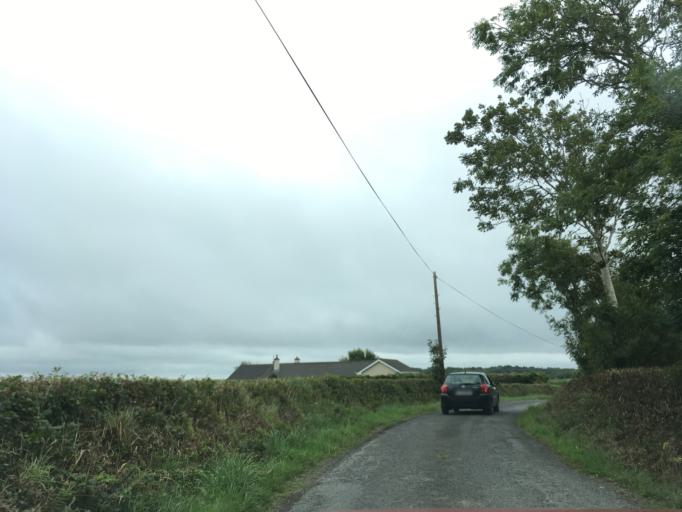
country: IE
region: Munster
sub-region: An Clar
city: Ennis
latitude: 52.7205
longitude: -9.0949
